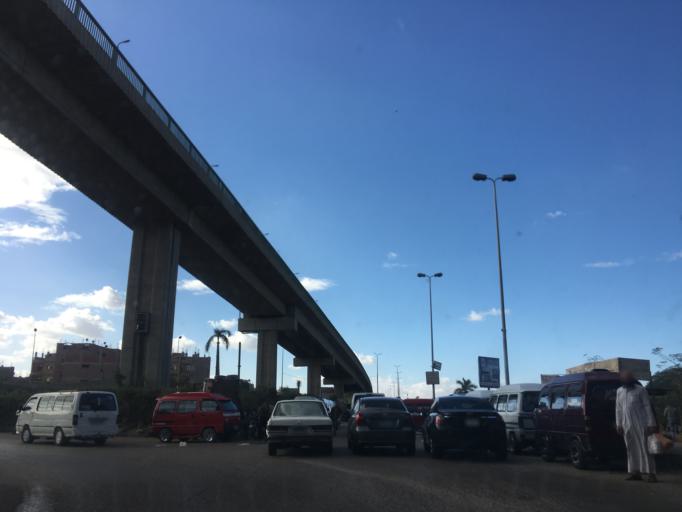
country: EG
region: Al Jizah
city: Al Jizah
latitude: 30.0302
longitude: 31.1631
